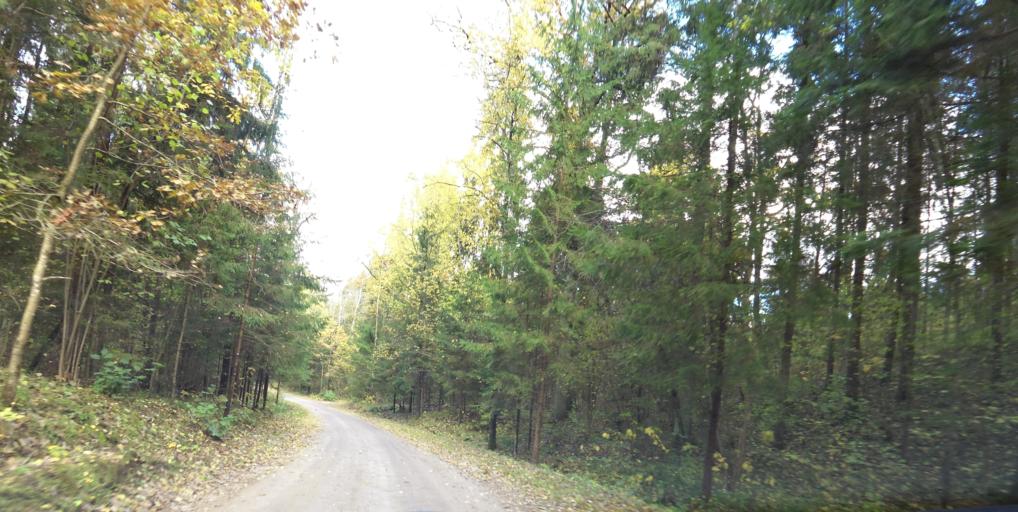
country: LT
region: Vilnius County
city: Vilkpede
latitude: 54.6525
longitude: 25.2557
